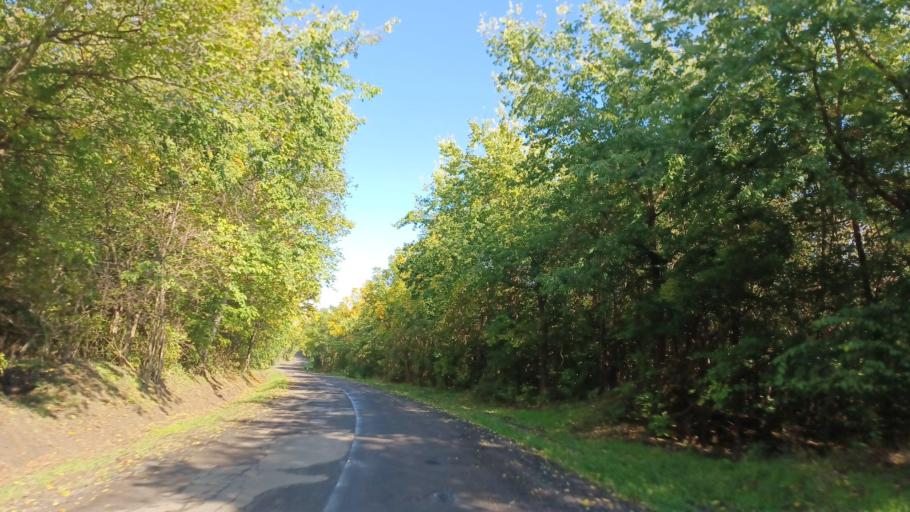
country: HU
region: Tolna
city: Szedres
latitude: 46.5341
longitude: 18.5930
